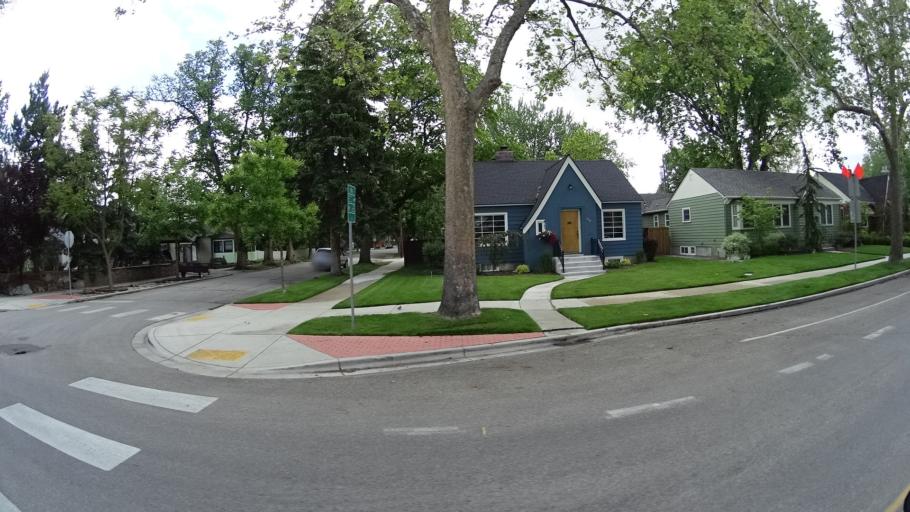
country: US
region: Idaho
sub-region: Ada County
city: Boise
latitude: 43.6337
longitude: -116.2059
